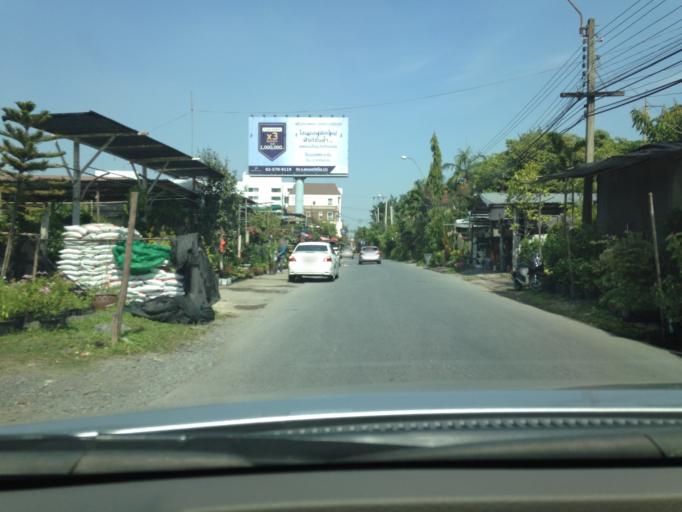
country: TH
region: Bangkok
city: Lat Phrao
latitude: 13.8321
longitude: 100.6298
